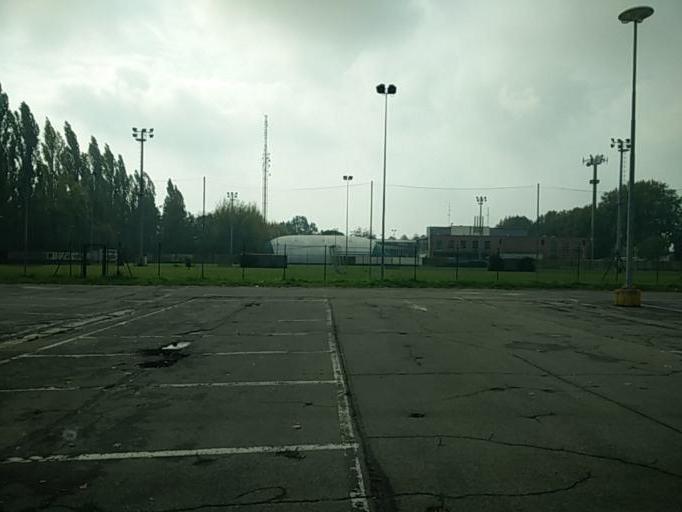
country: IT
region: Emilia-Romagna
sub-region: Provincia di Modena
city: Carpi Centro
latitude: 44.7841
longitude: 10.8678
